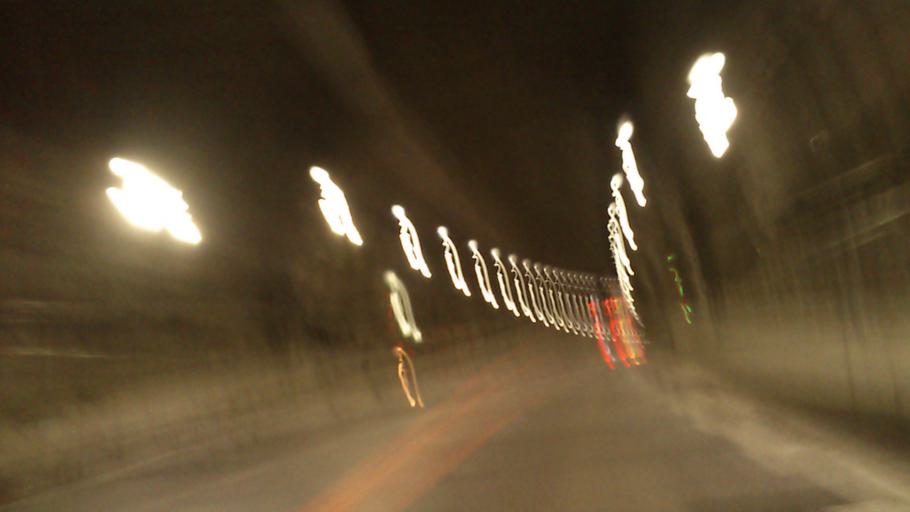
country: JP
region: Nagano
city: Iida
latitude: 35.4580
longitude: 137.6725
